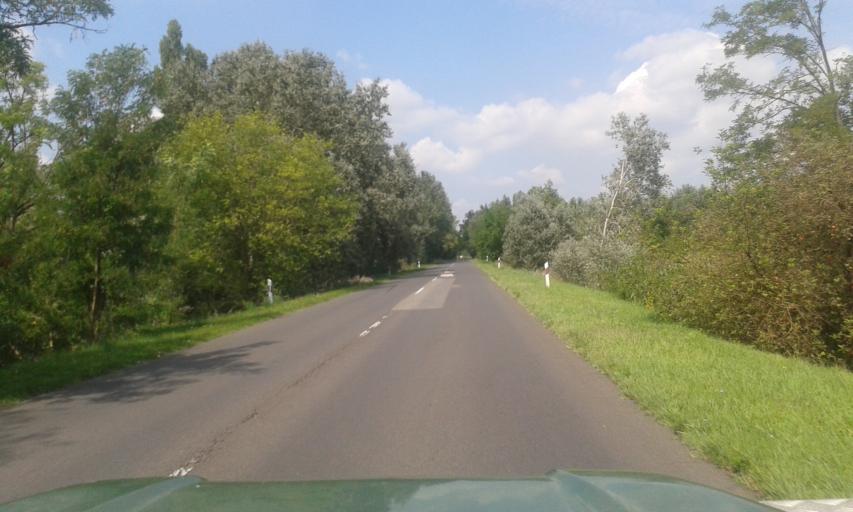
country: HU
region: Csongrad
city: Szatymaz
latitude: 46.3773
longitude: 20.0406
